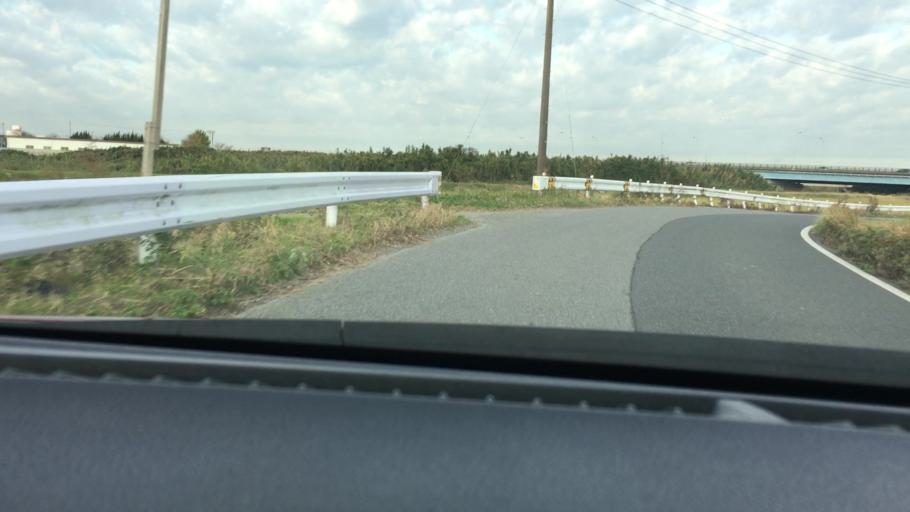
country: JP
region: Chiba
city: Kisarazu
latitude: 35.4079
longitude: 139.9543
